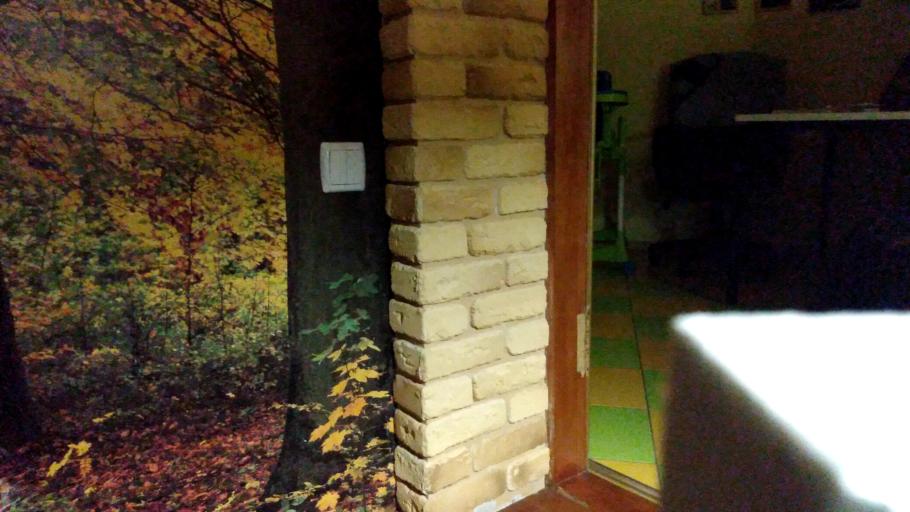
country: RU
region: Vologda
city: Lipin Bor
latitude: 61.1392
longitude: 37.9106
